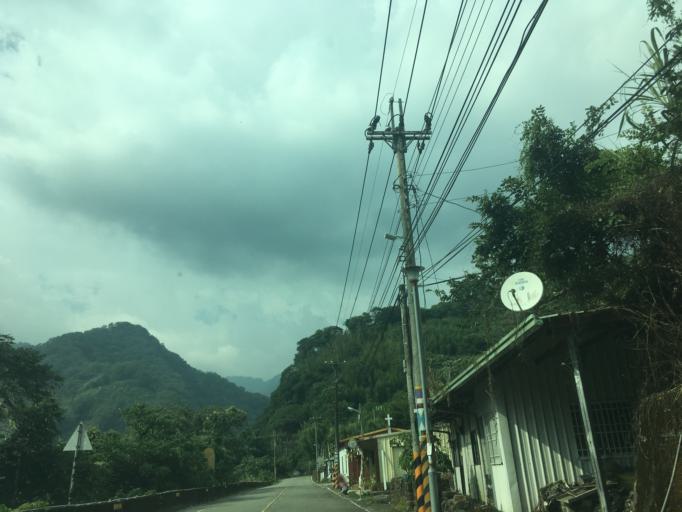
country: TW
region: Taiwan
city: Fengyuan
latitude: 24.3398
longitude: 120.9354
